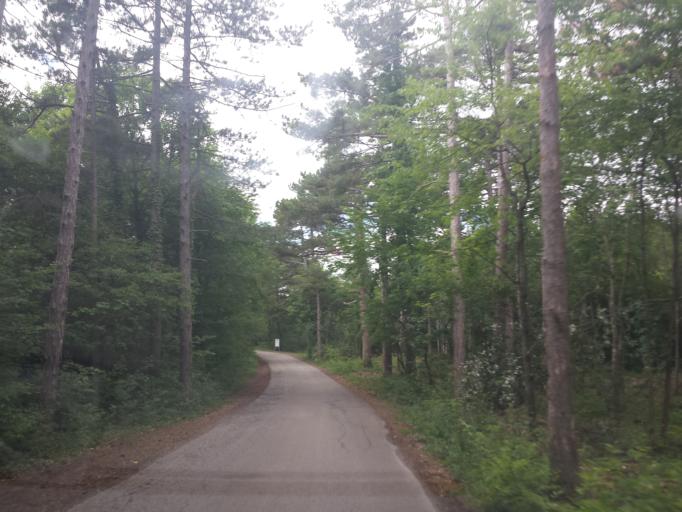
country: AT
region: Lower Austria
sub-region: Politischer Bezirk Baden
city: Hirtenberg
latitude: 47.9236
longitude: 16.1739
